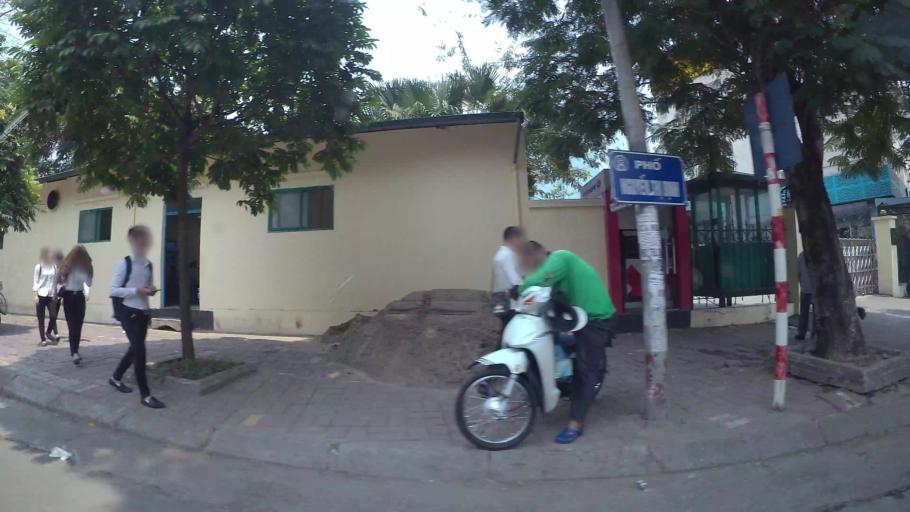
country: VN
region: Ha Noi
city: Thanh Xuan
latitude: 21.0087
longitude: 105.8048
